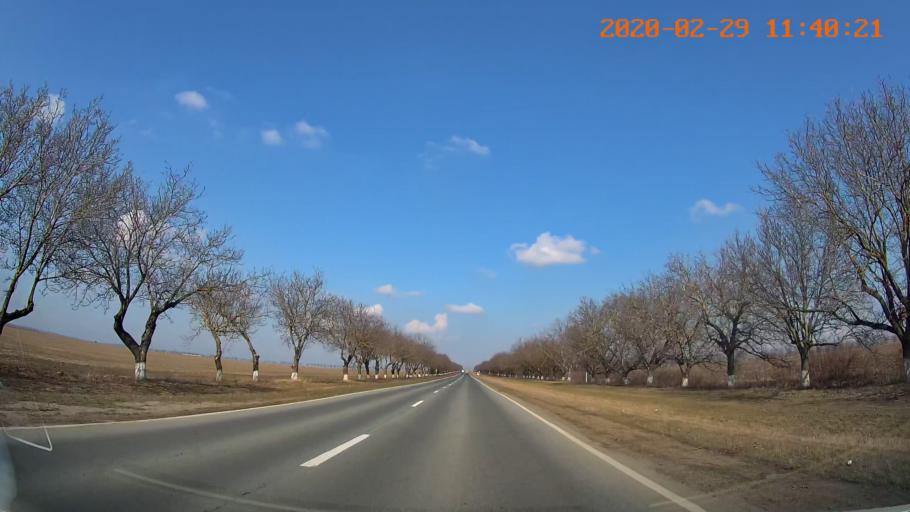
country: MD
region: Rezina
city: Saharna
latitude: 47.6549
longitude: 29.0206
